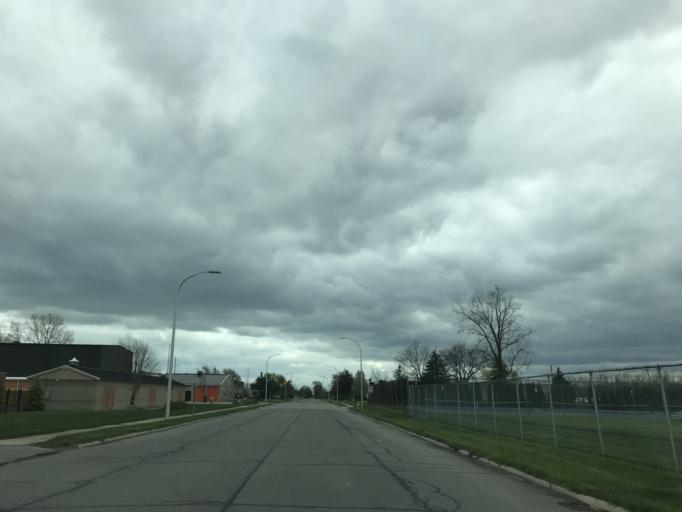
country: US
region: Michigan
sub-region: Wayne County
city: Riverview
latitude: 42.1753
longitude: -83.1743
